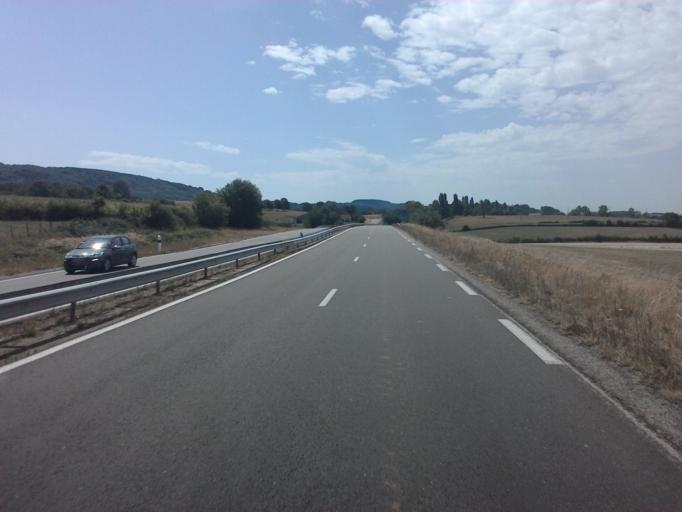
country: FR
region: Bourgogne
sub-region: Departement de Saone-et-Loire
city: Cuiseaux
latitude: 46.5084
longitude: 5.3875
